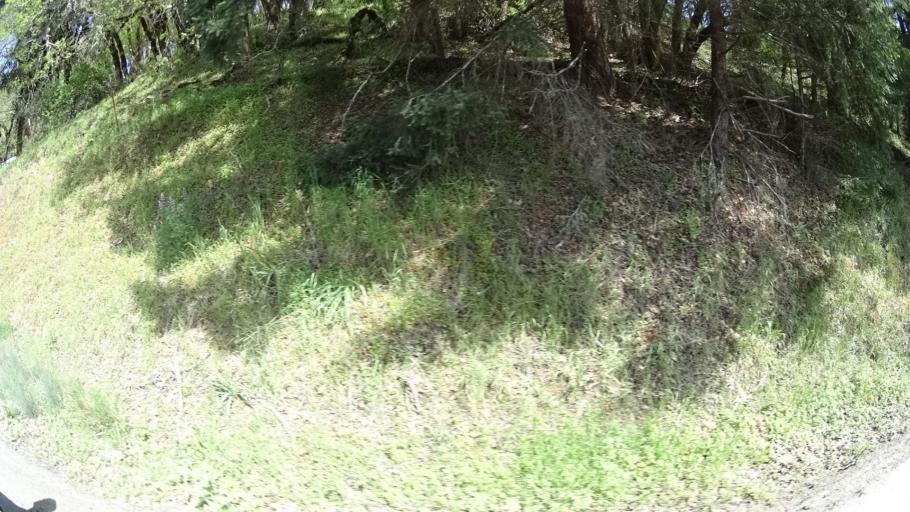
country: US
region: California
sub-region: Humboldt County
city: Redway
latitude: 40.4021
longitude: -123.7464
